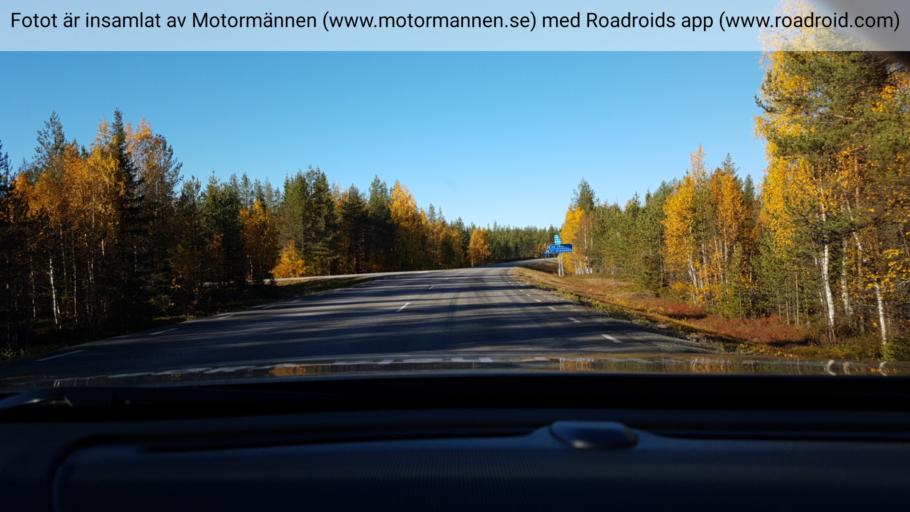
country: SE
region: Vaesterbotten
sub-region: Norsjo Kommun
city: Norsjoe
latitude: 65.4092
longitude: 19.7489
